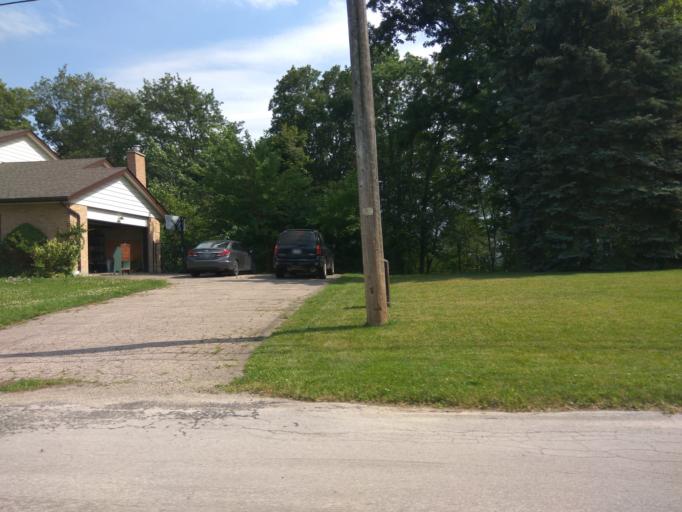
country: CA
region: Ontario
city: Cambridge
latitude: 43.4047
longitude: -80.4003
